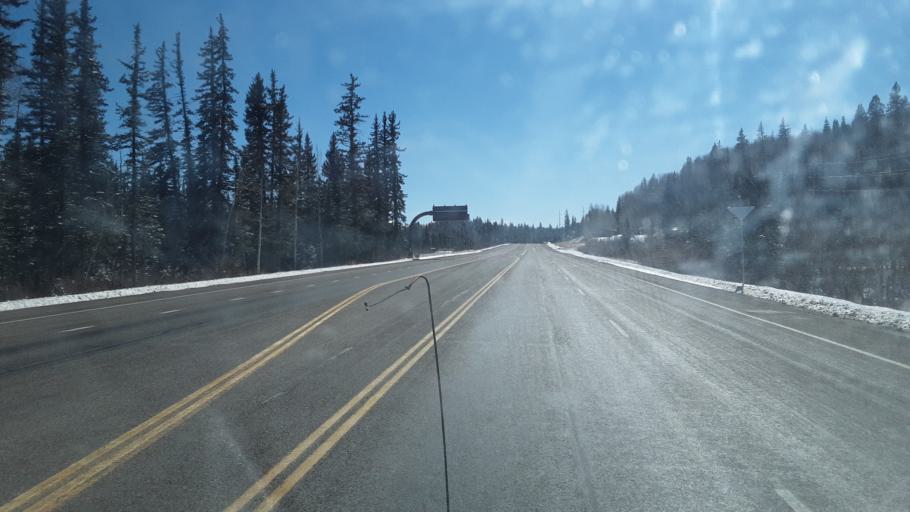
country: US
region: Colorado
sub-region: San Juan County
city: Silverton
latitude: 37.6207
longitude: -107.8121
